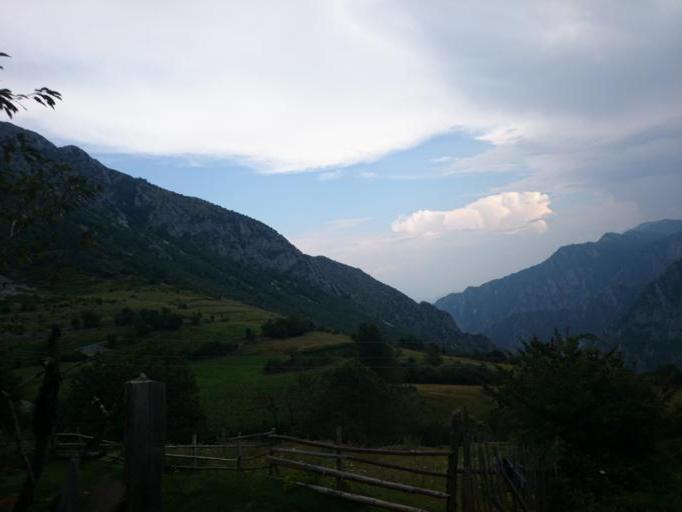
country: AL
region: Diber
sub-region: Rrethi i Dibres
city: Fushe-Lure
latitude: 41.7698
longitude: 20.2271
